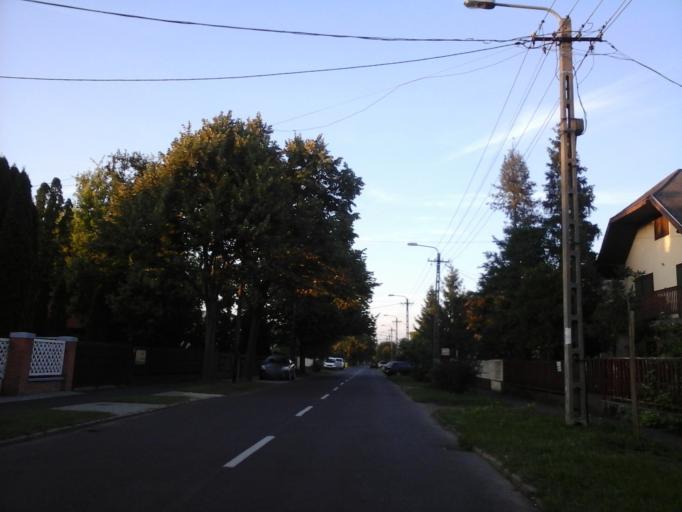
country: HU
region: Hajdu-Bihar
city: Hajduszoboszlo
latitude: 47.4563
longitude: 21.4085
